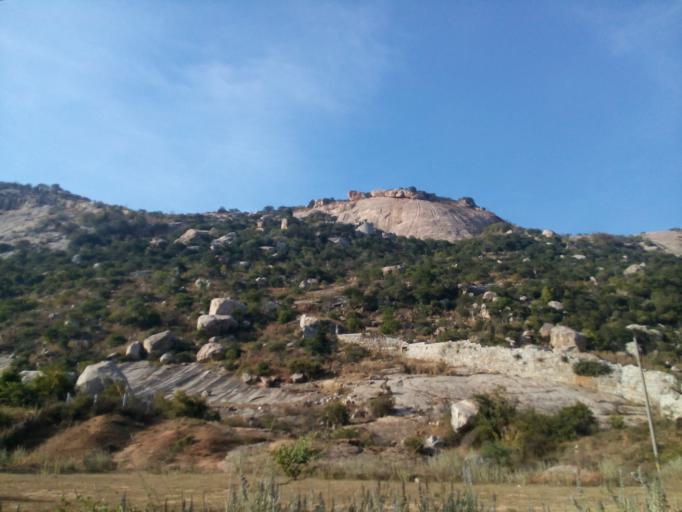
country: IN
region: Andhra Pradesh
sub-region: Chittoor
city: Narasingapuram
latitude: 13.5813
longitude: 79.3010
